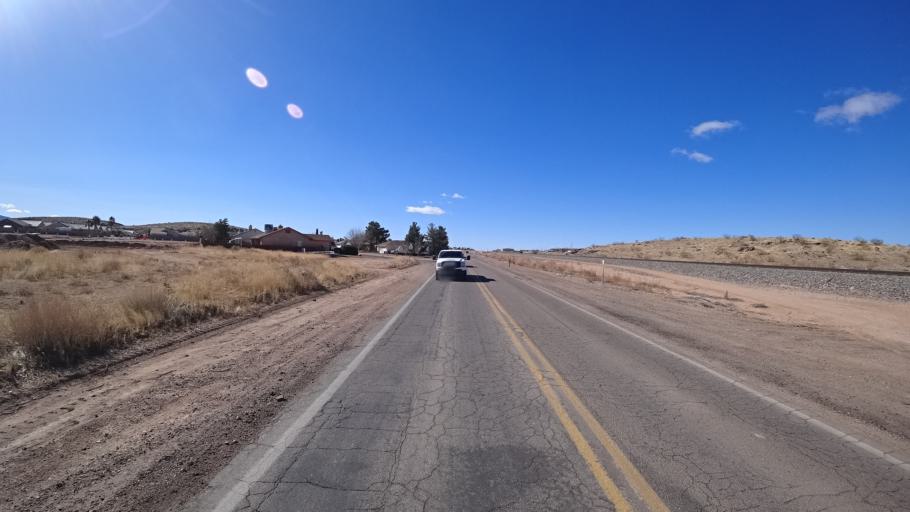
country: US
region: Arizona
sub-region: Mohave County
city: Kingman
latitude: 35.2157
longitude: -114.0082
